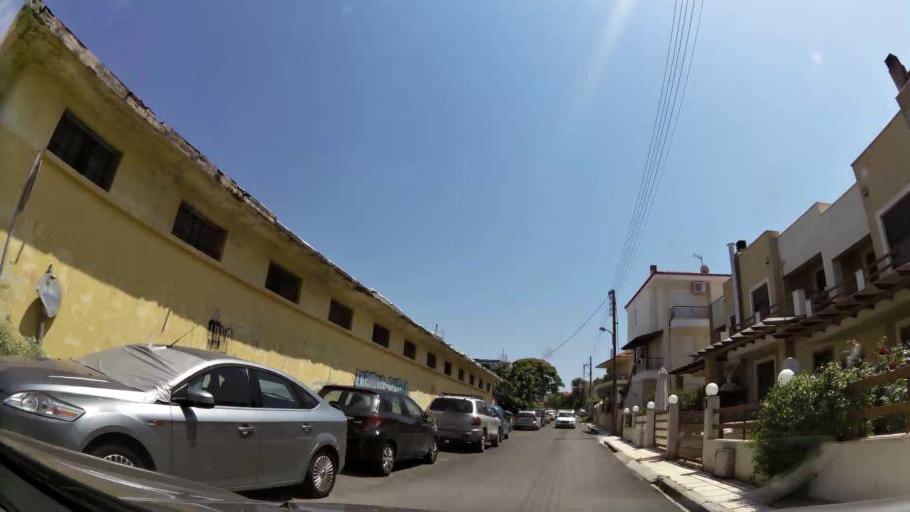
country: GR
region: Central Macedonia
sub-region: Nomos Thessalonikis
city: Trilofos
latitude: 40.4718
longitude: 22.9724
